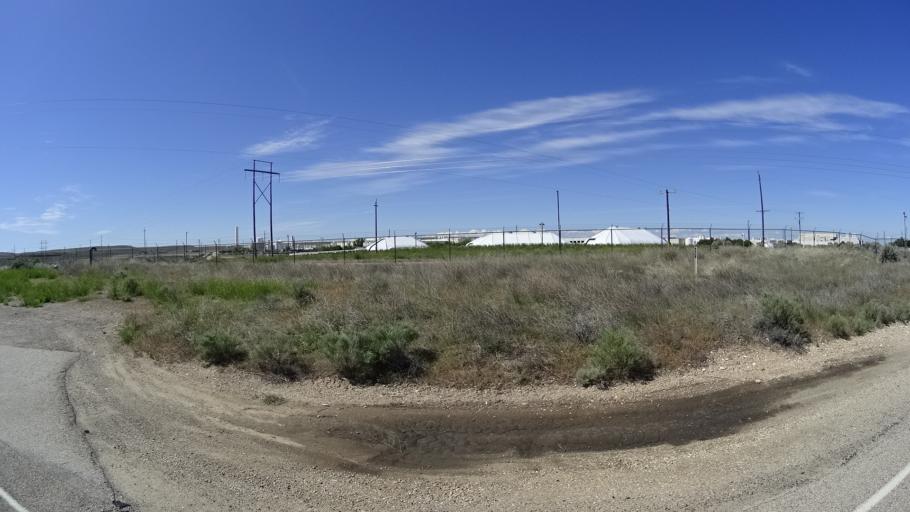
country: US
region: Idaho
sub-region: Ada County
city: Boise
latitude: 43.5312
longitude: -116.1395
